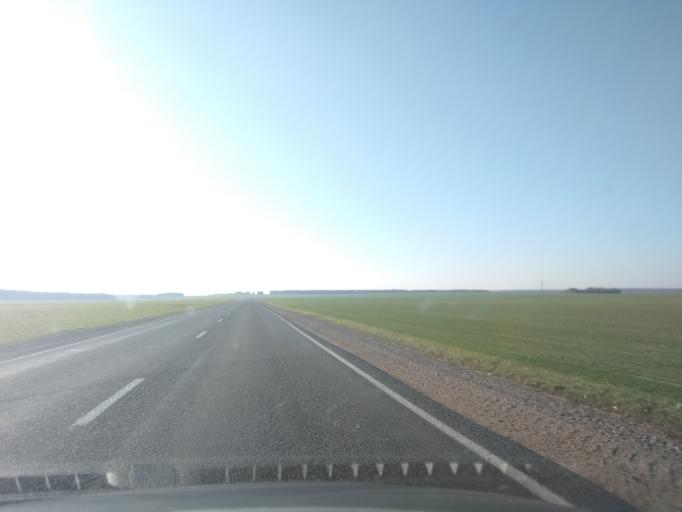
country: BY
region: Grodnenskaya
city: Svislach
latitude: 53.1308
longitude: 24.1777
